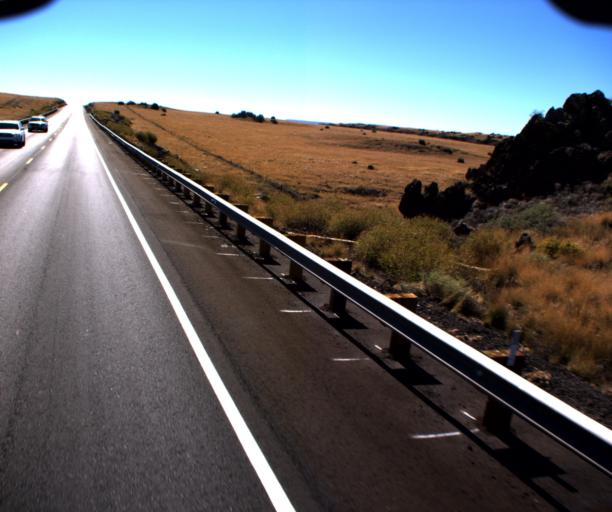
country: US
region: Arizona
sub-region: Apache County
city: Springerville
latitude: 34.2495
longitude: -109.3506
